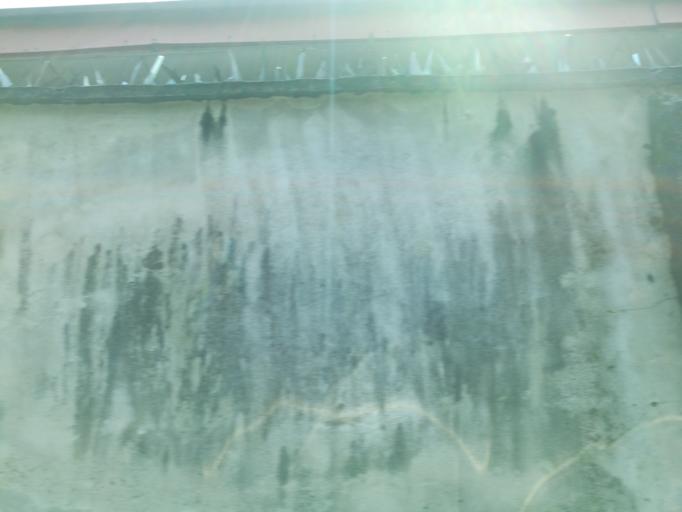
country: NG
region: Rivers
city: Port Harcourt
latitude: 4.8085
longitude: 6.9841
